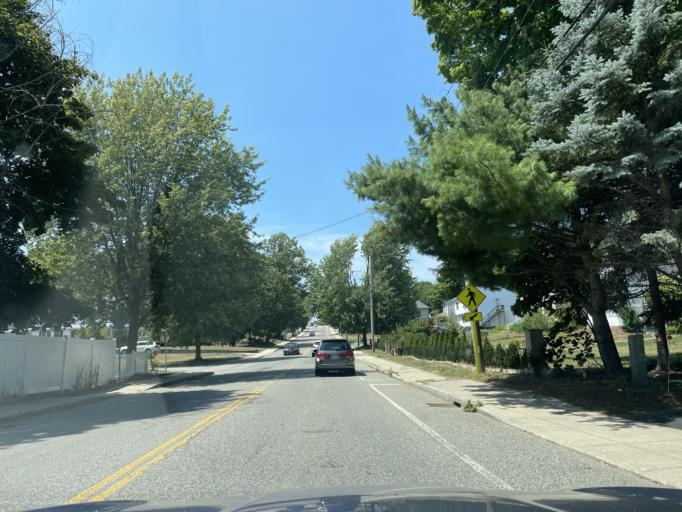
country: US
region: Massachusetts
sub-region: Norfolk County
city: Randolph
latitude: 42.1602
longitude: -71.0374
